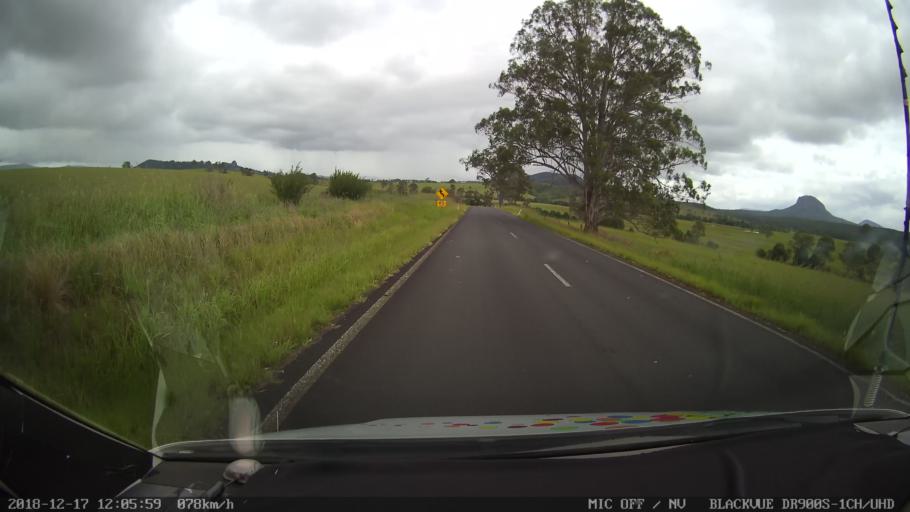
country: AU
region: New South Wales
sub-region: Kyogle
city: Kyogle
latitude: -28.4869
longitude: 152.5680
